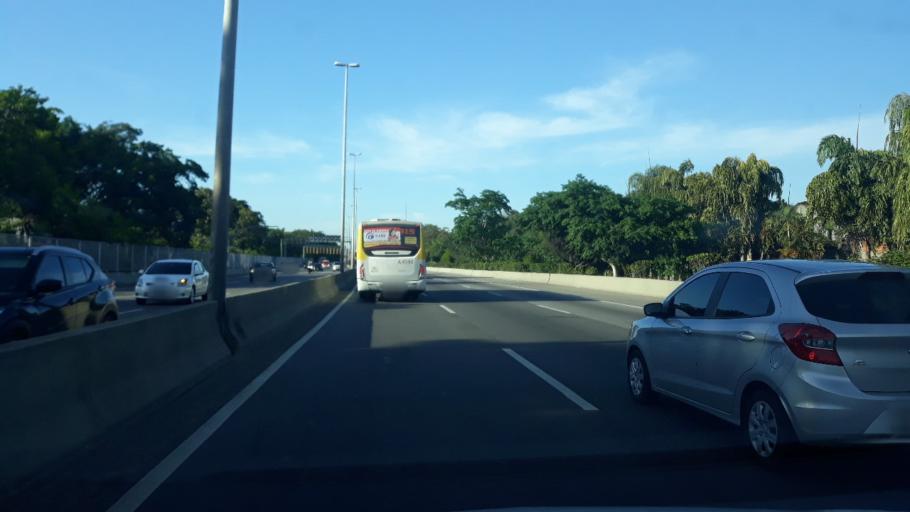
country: BR
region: Rio de Janeiro
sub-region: Sao Joao De Meriti
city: Sao Joao de Meriti
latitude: -22.9442
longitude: -43.3535
